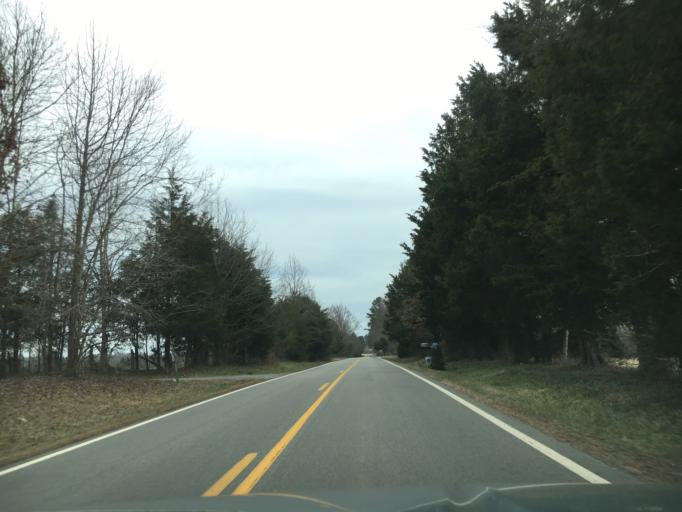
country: US
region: Virginia
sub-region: Charlotte County
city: Charlotte Court House
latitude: 37.0078
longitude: -78.6980
